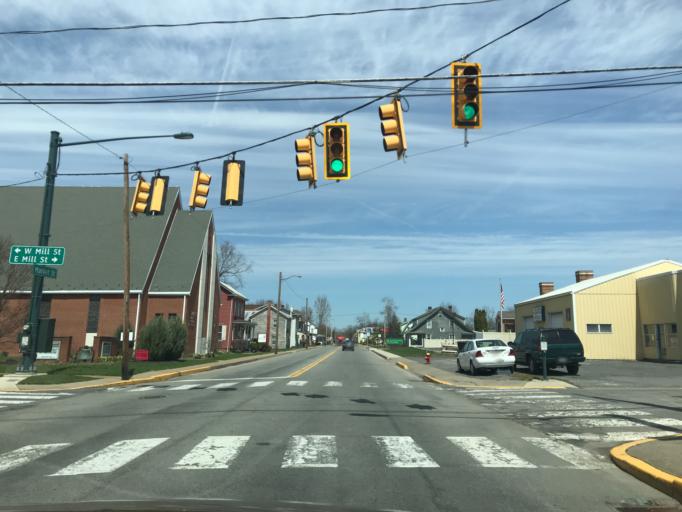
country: US
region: Pennsylvania
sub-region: Snyder County
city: Selinsgrove
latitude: 40.8038
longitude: -76.8599
